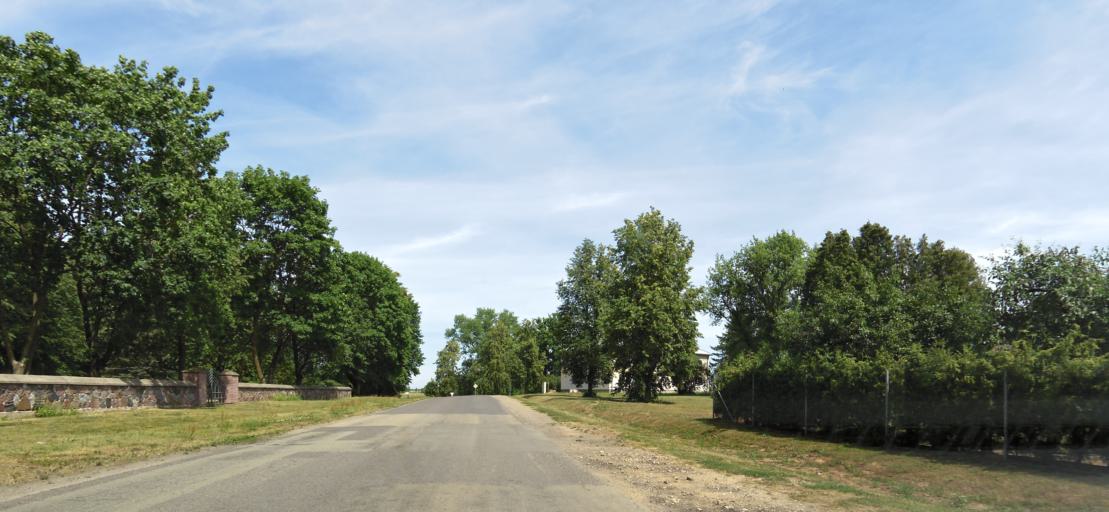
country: LT
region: Panevezys
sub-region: Panevezys City
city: Panevezys
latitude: 55.6528
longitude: 24.2300
